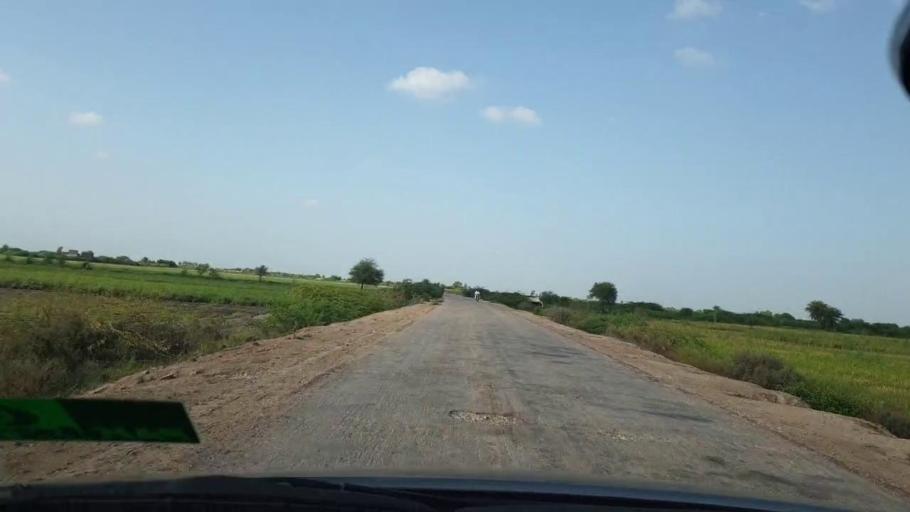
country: PK
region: Sindh
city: Tando Bago
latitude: 24.7017
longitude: 69.1911
